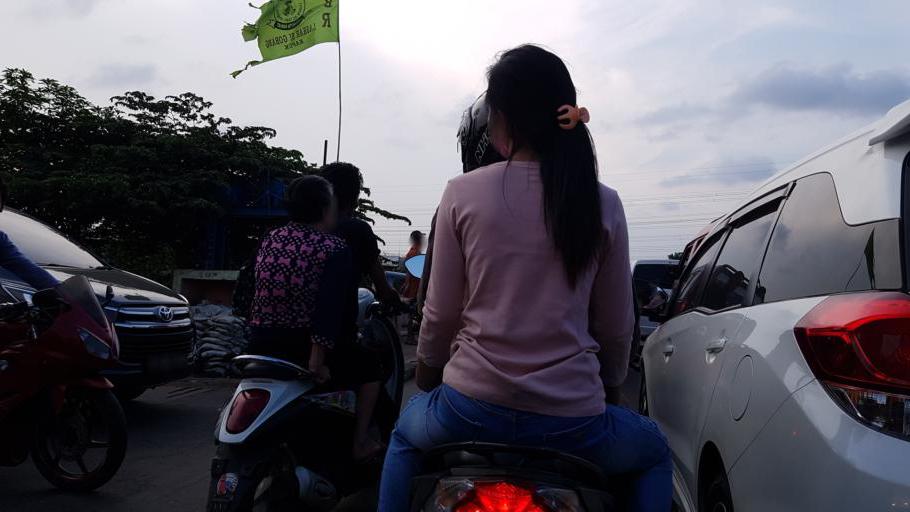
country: ID
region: West Java
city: Ciputat
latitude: -6.1354
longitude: 106.7532
